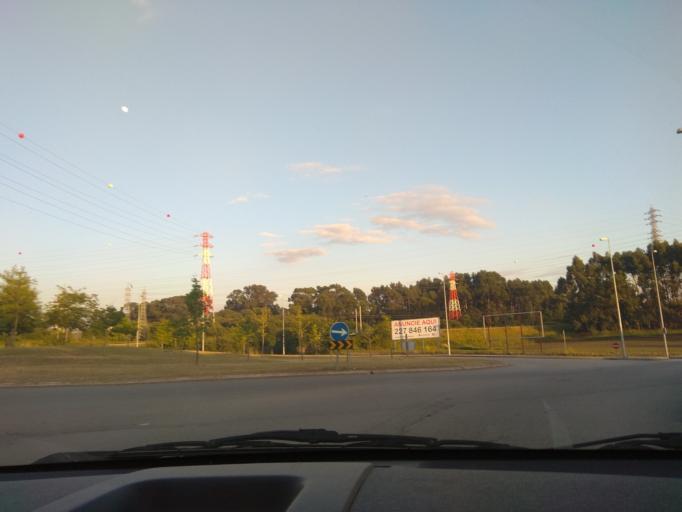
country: PT
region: Porto
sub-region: Matosinhos
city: Senhora da Hora
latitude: 41.2007
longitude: -8.6525
